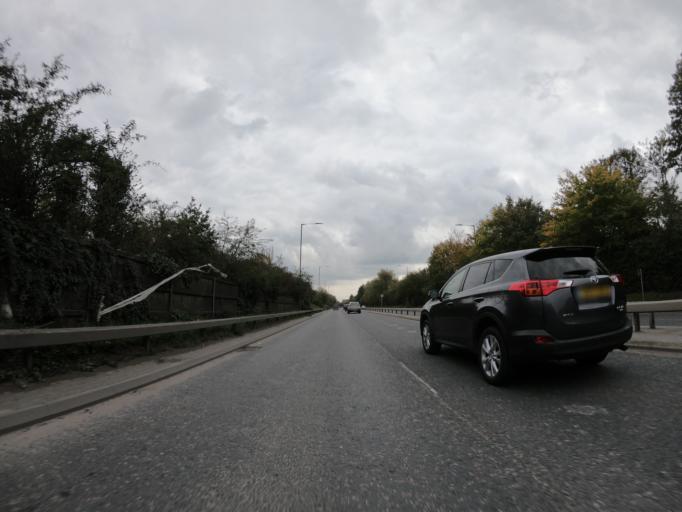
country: GB
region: England
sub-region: Greater London
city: Erith
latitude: 51.4865
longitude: 0.1697
